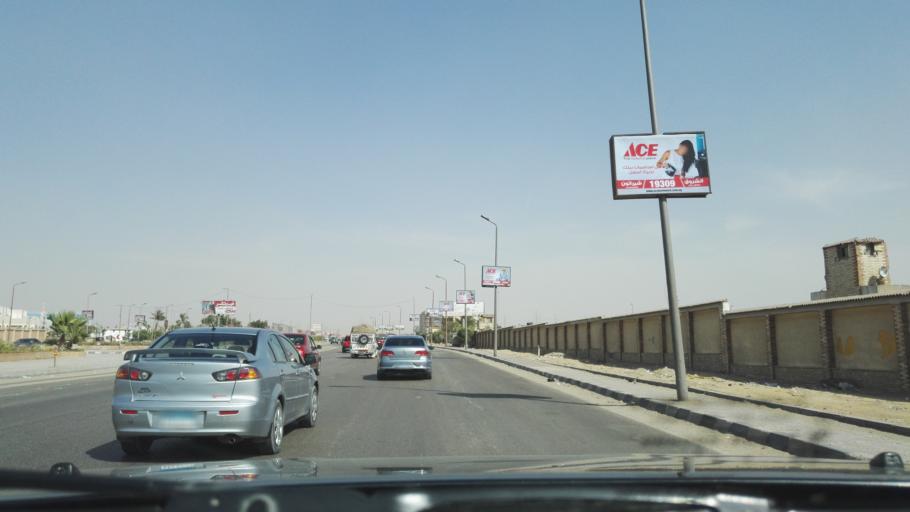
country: EG
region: Muhafazat al Qalyubiyah
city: Al Khankah
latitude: 30.0805
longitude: 31.4157
